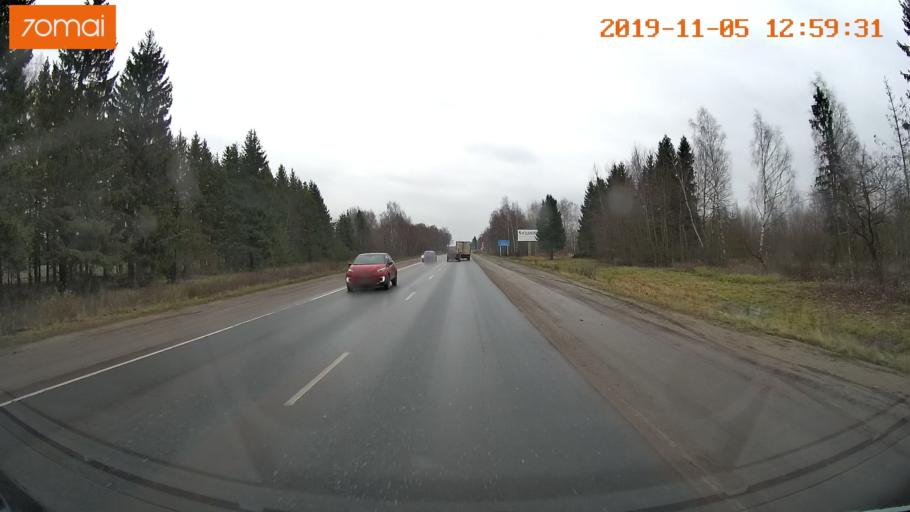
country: RU
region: Ivanovo
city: Kokhma
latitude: 56.9180
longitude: 41.1307
